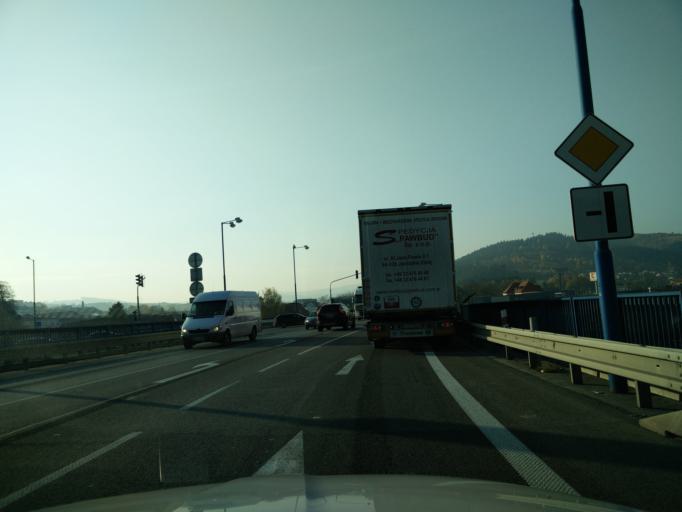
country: SK
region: Zilinsky
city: Cadca
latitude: 49.4396
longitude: 18.7941
